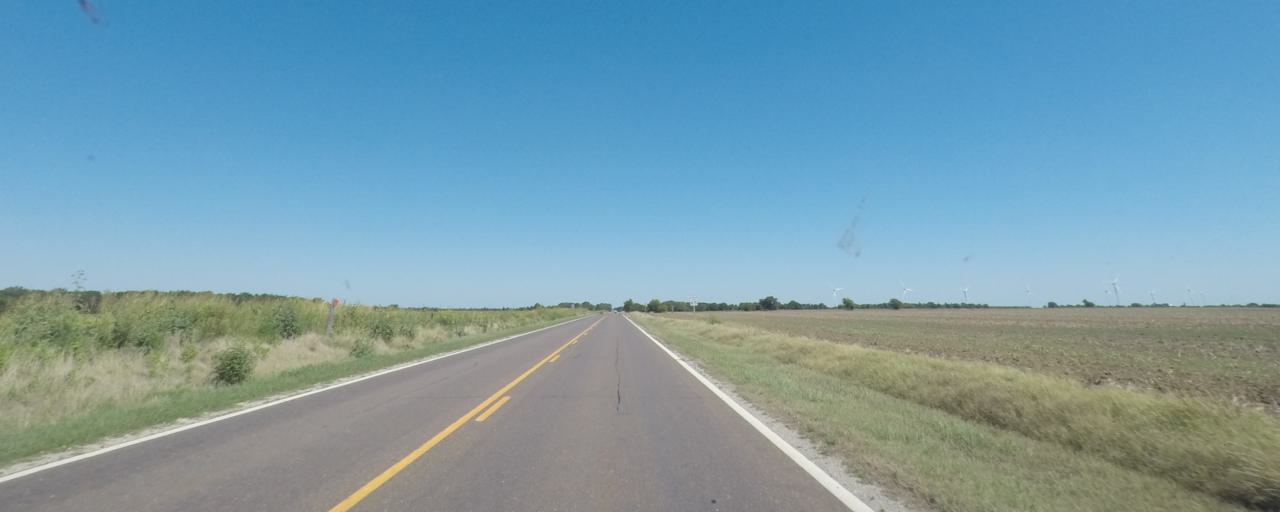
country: US
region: Kansas
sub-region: Sumner County
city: Wellington
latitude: 37.1173
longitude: -97.4017
